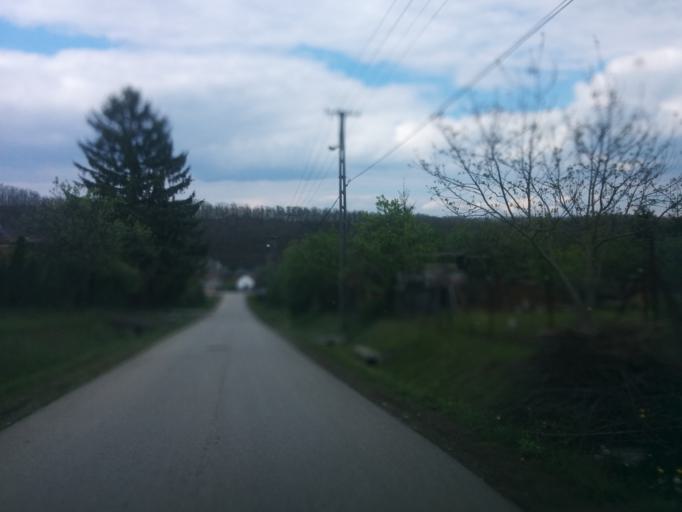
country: HU
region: Nograd
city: Retsag
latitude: 47.8839
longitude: 19.1376
